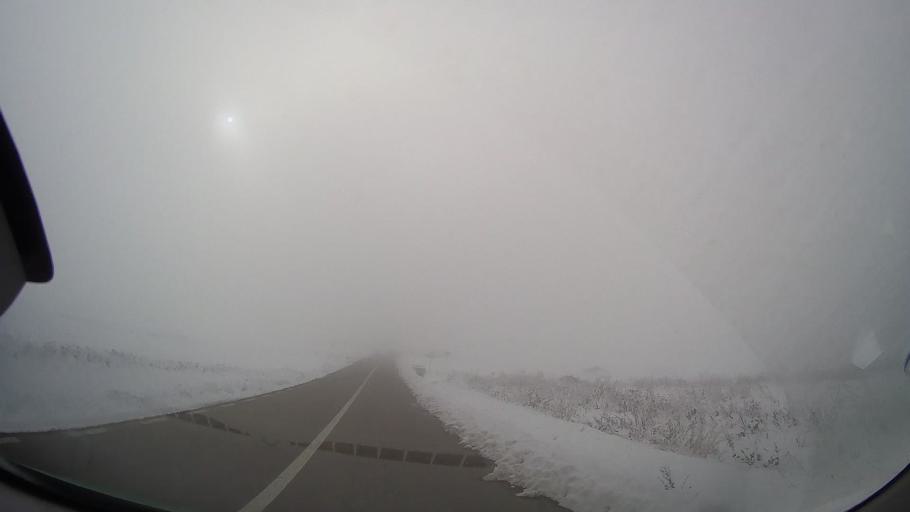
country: RO
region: Iasi
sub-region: Comuna Valea Seaca
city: Topile
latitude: 47.2717
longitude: 26.6702
